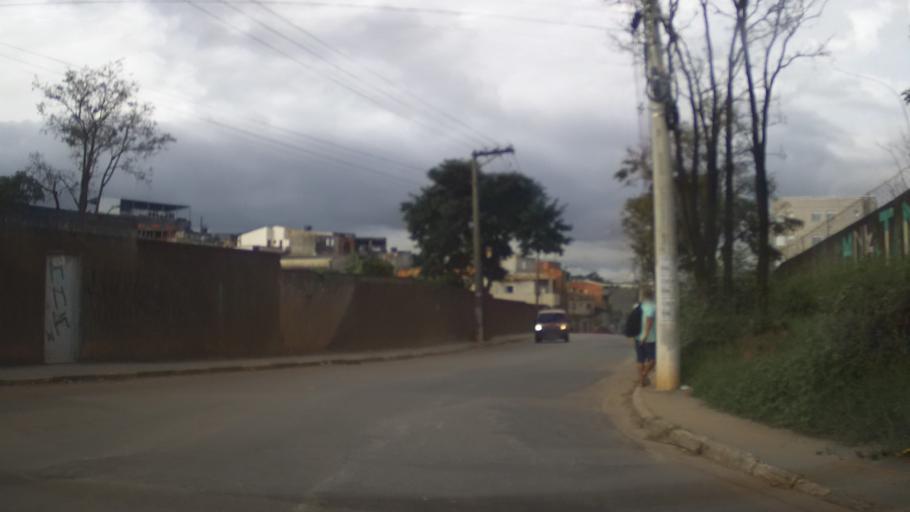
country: BR
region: Sao Paulo
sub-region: Itaquaquecetuba
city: Itaquaquecetuba
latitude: -23.4554
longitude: -46.4320
